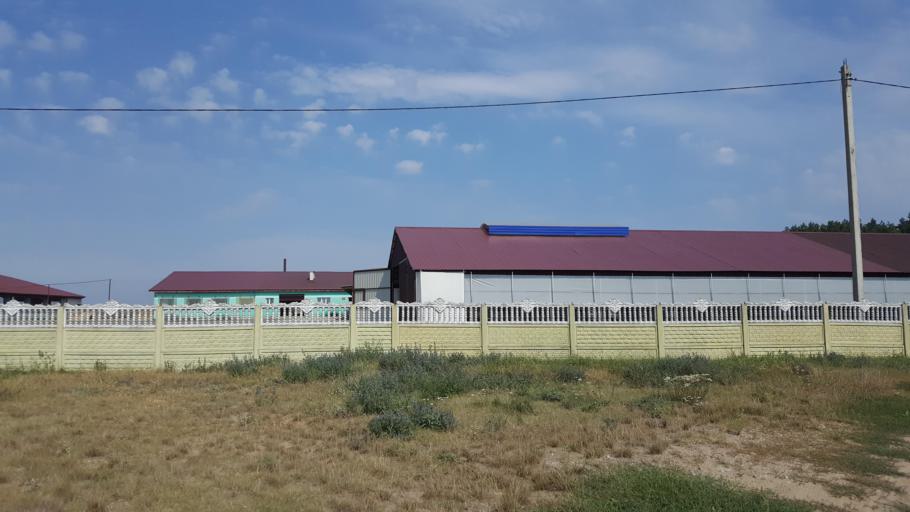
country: BY
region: Brest
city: Kamyanyuki
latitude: 52.4827
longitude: 23.7201
